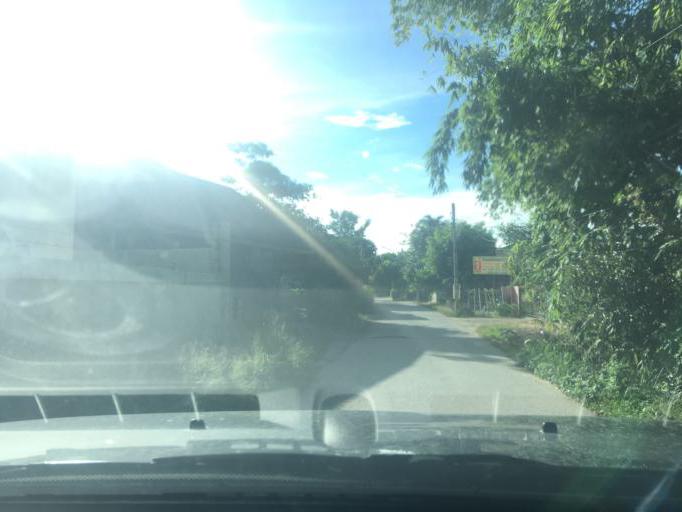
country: TH
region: Chiang Mai
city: San Sai
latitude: 18.9638
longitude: 98.9795
